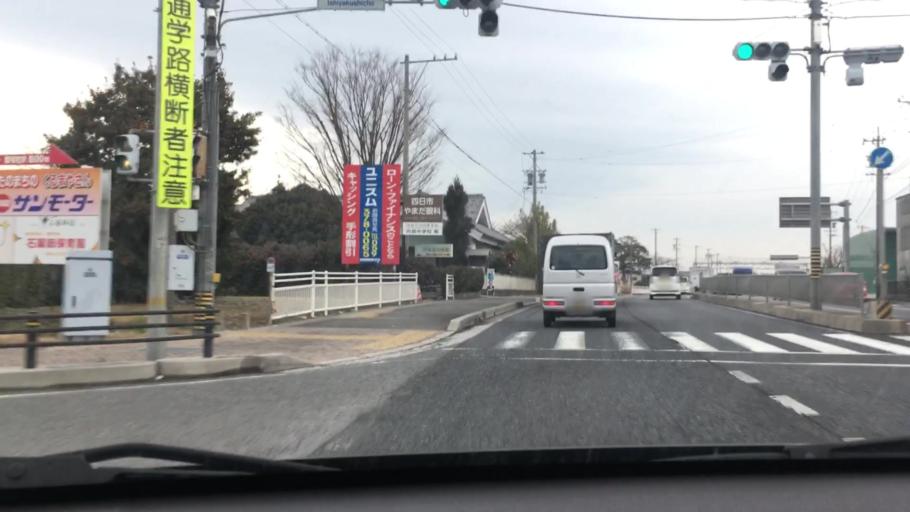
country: JP
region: Mie
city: Suzuka
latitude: 34.9027
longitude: 136.5486
